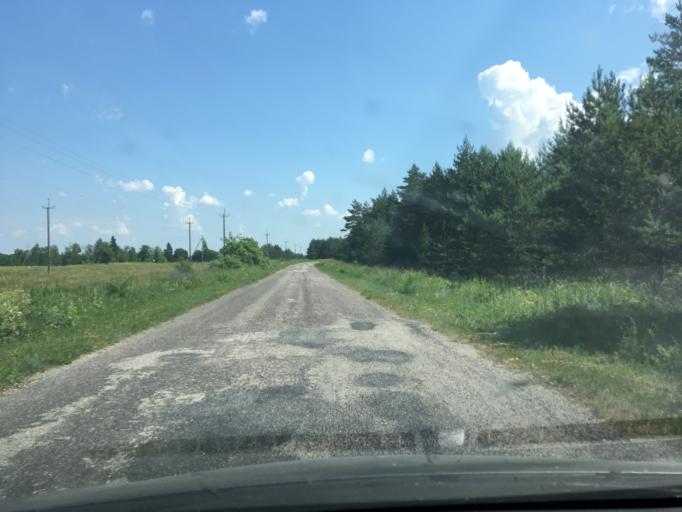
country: EE
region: Laeaene
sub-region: Lihula vald
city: Lihula
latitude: 58.6659
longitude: 23.7485
